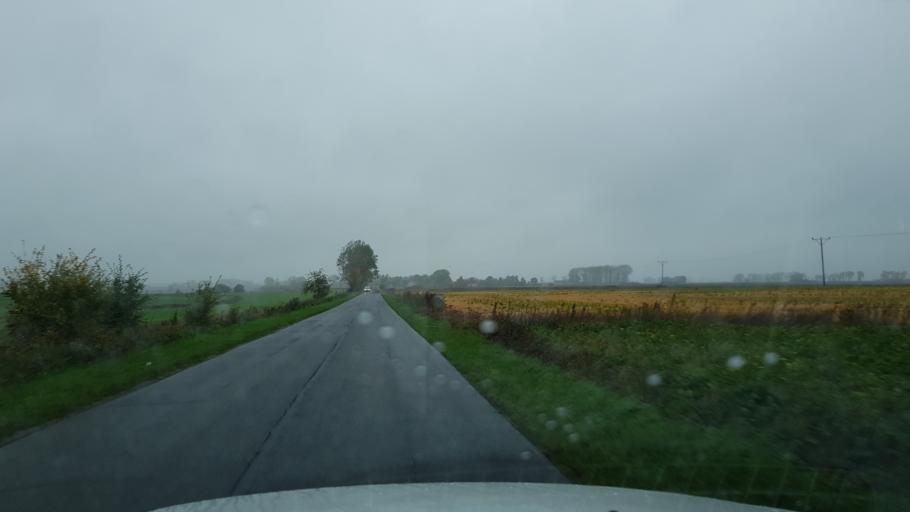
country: PL
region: West Pomeranian Voivodeship
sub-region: Powiat pyrzycki
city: Pyrzyce
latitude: 53.1581
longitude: 14.8599
